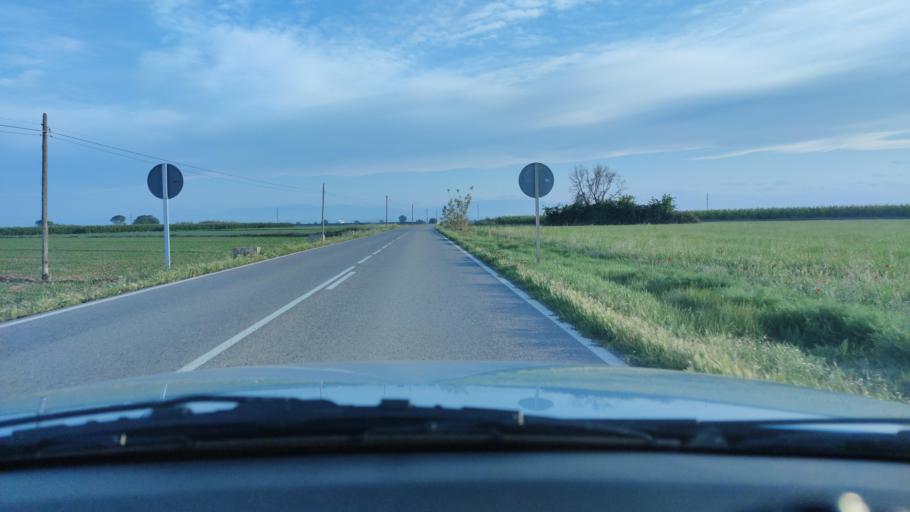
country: ES
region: Catalonia
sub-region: Provincia de Lleida
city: Castellnou de Seana
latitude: 41.6526
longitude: 0.9971
